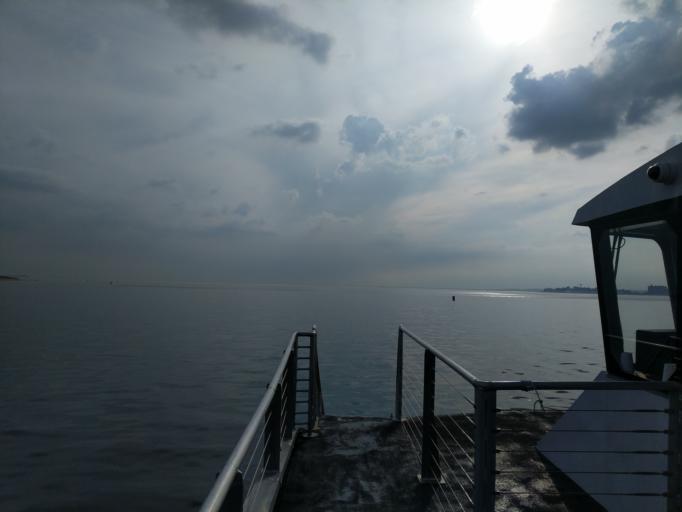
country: US
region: New York
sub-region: Kings County
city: Coney Island
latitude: 40.5638
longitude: -73.9280
